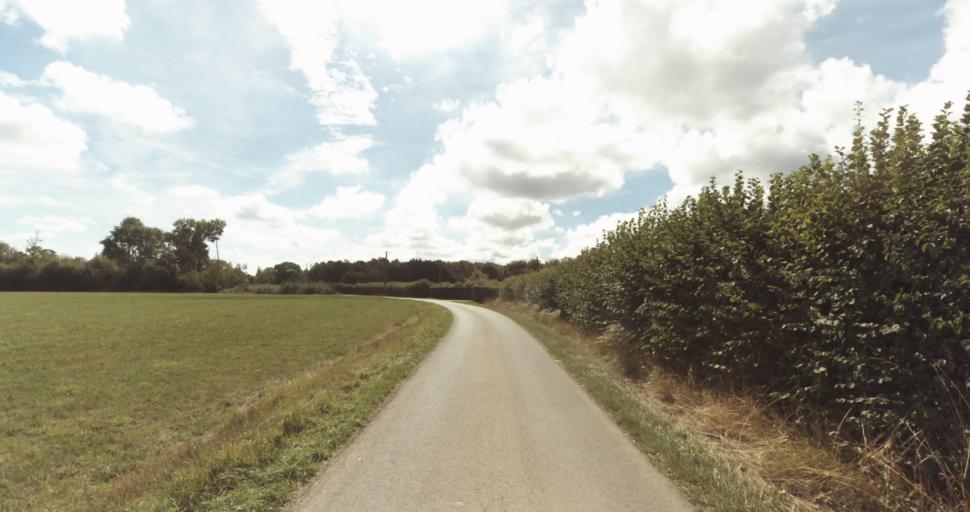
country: FR
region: Lower Normandy
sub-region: Departement de l'Orne
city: Vimoutiers
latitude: 48.9516
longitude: 0.3111
